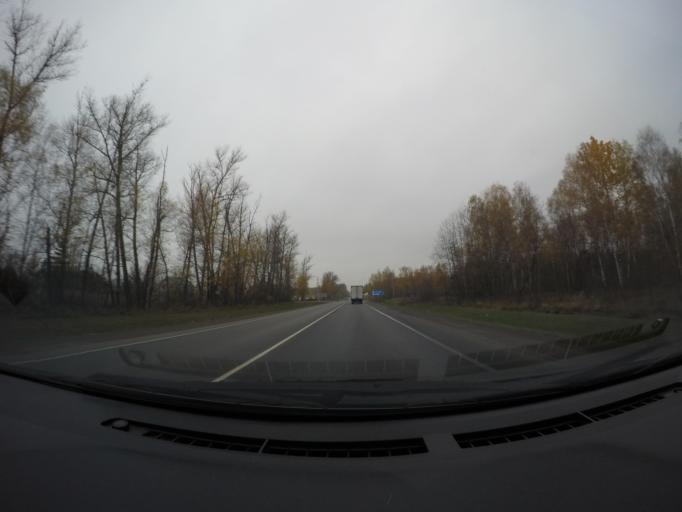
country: RU
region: Moskovskaya
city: Bronnitsy
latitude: 55.3722
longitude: 38.1230
